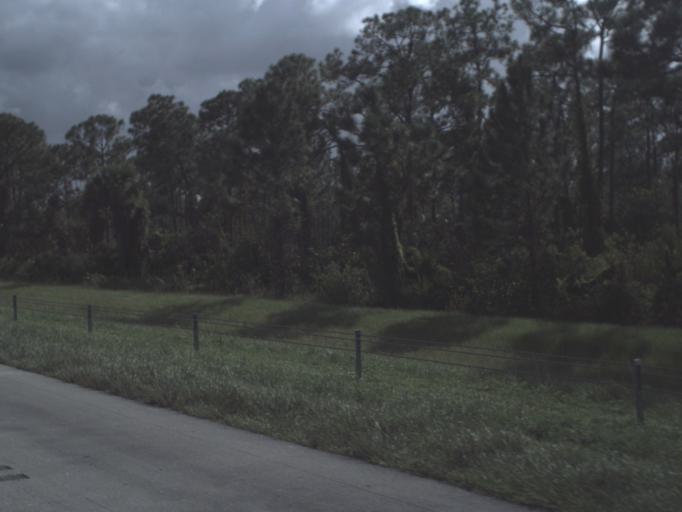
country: US
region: Florida
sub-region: Martin County
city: Port Salerno
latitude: 27.0916
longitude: -80.2557
